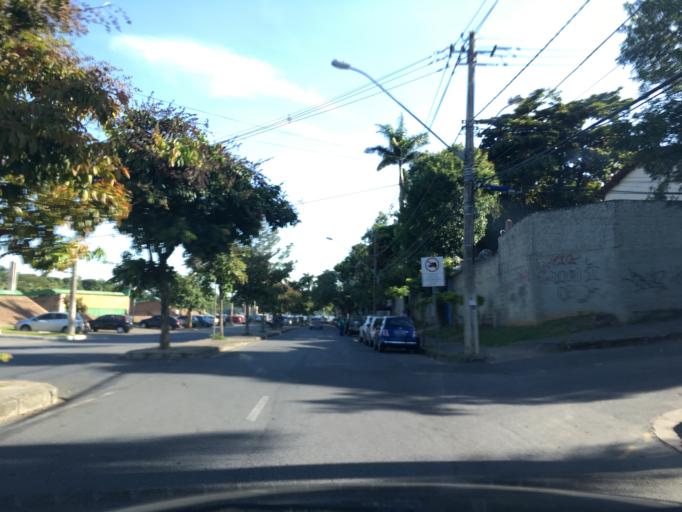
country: BR
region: Minas Gerais
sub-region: Belo Horizonte
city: Belo Horizonte
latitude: -19.8618
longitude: -43.9815
